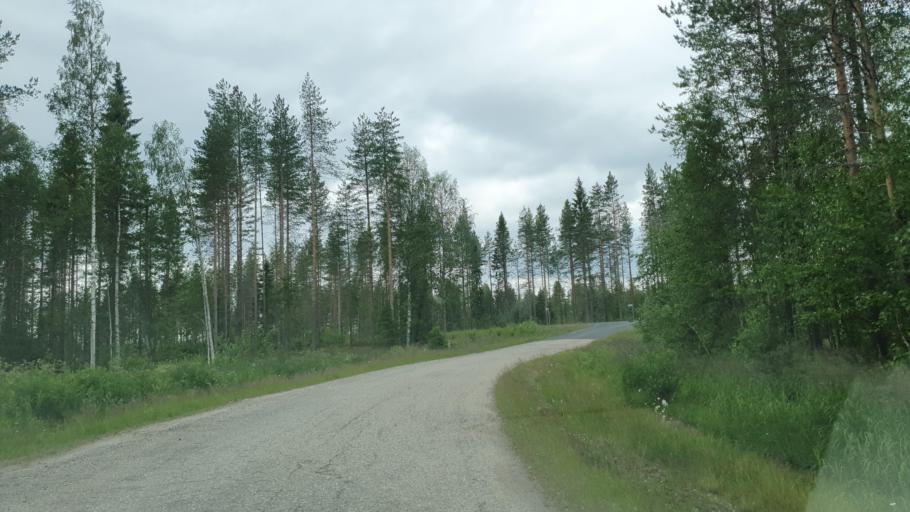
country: FI
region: Kainuu
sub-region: Kehys-Kainuu
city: Kuhmo
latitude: 64.0116
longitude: 29.3385
